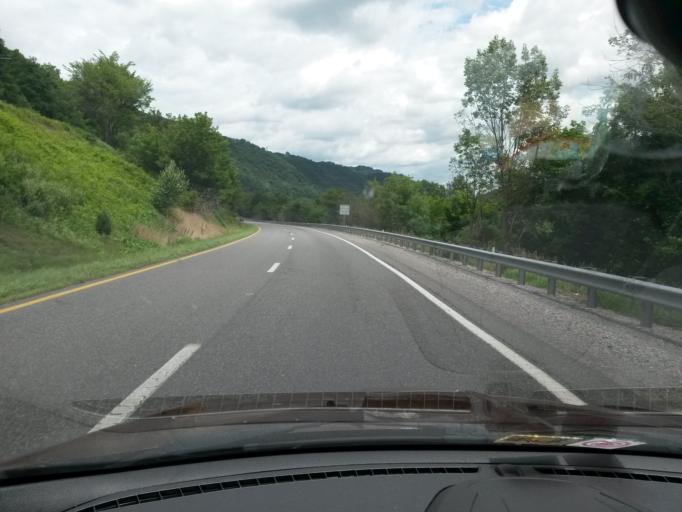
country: US
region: Virginia
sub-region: Giles County
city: Narrows
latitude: 37.3753
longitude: -80.8498
